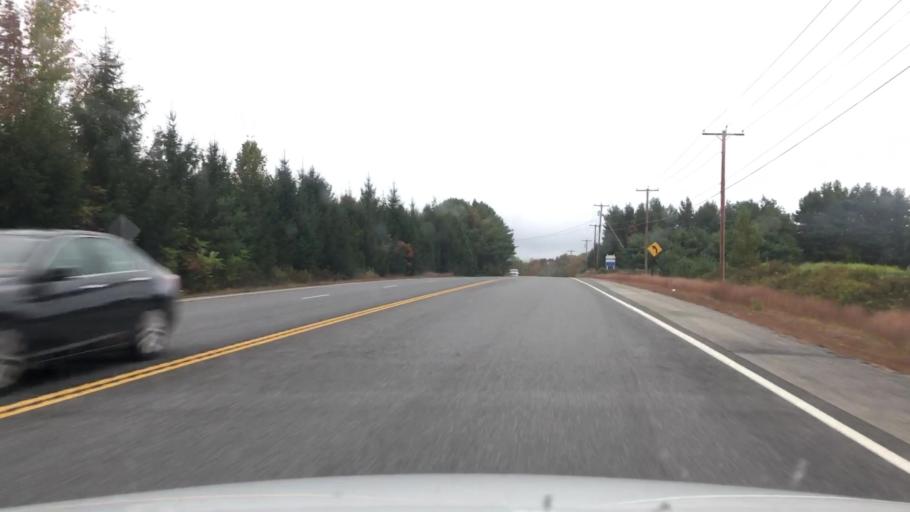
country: US
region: Maine
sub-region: Androscoggin County
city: Poland
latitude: 44.0038
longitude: -70.3632
